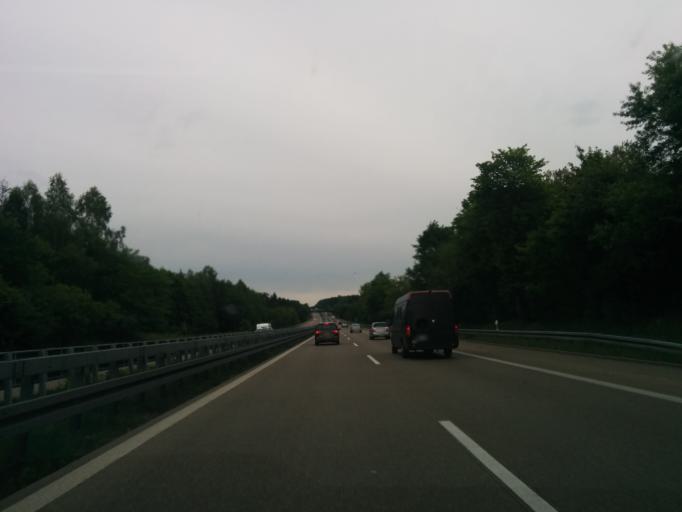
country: DE
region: Baden-Wuerttemberg
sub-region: Tuebingen Region
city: Setzingen
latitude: 48.5551
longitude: 10.1206
